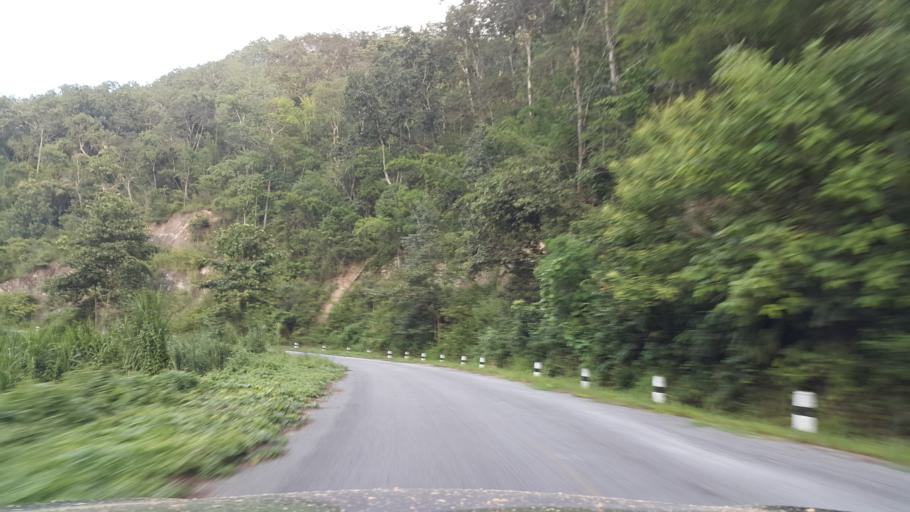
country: TH
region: Mae Hong Son
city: Mae Hi
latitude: 19.2064
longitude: 98.4317
